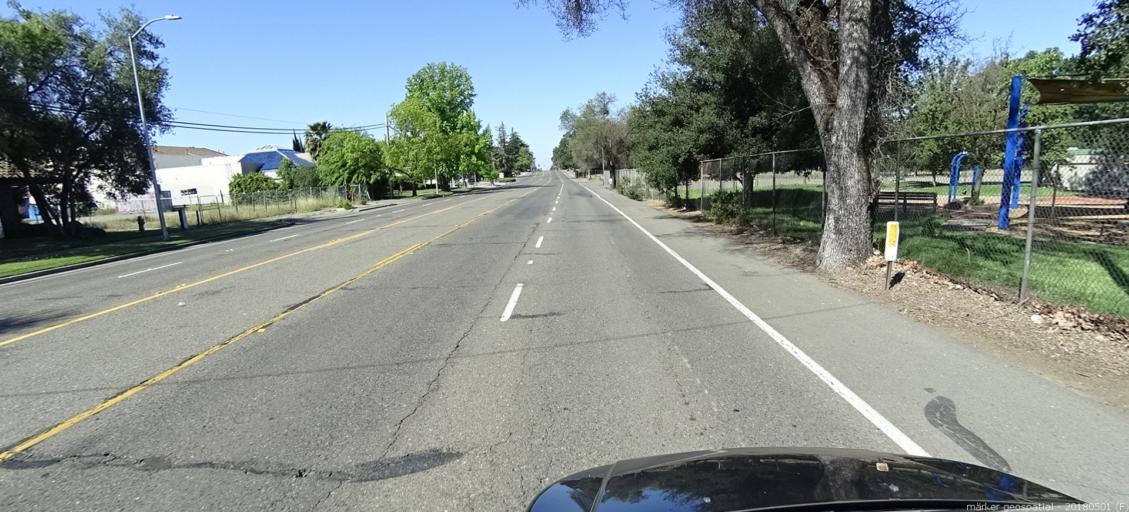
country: US
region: California
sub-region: Sacramento County
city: Arden-Arcade
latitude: 38.6398
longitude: -121.3762
